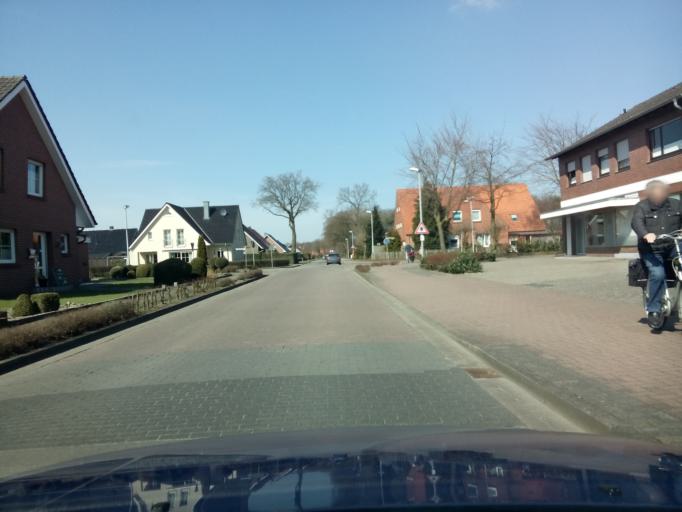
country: DE
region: Lower Saxony
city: Emlichheim
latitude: 52.6115
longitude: 6.8404
